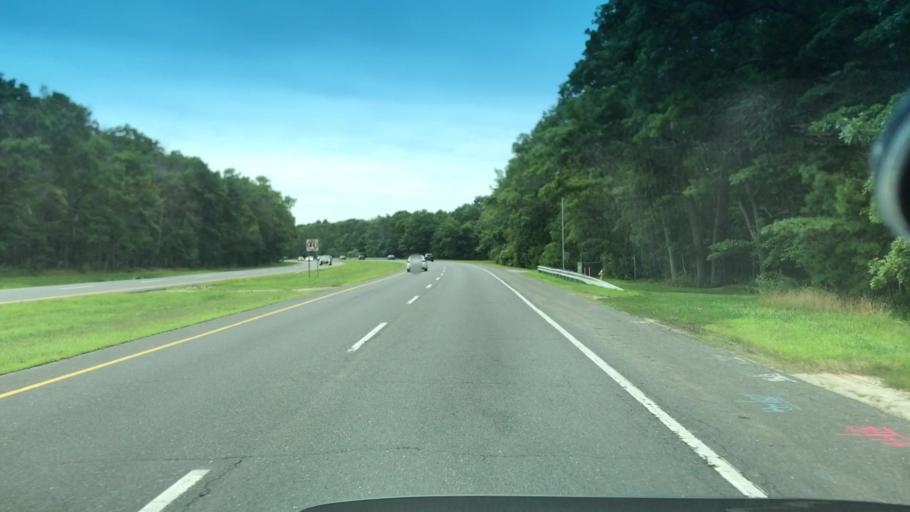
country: US
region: New York
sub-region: Suffolk County
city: Yaphank
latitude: 40.8586
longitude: -72.9013
